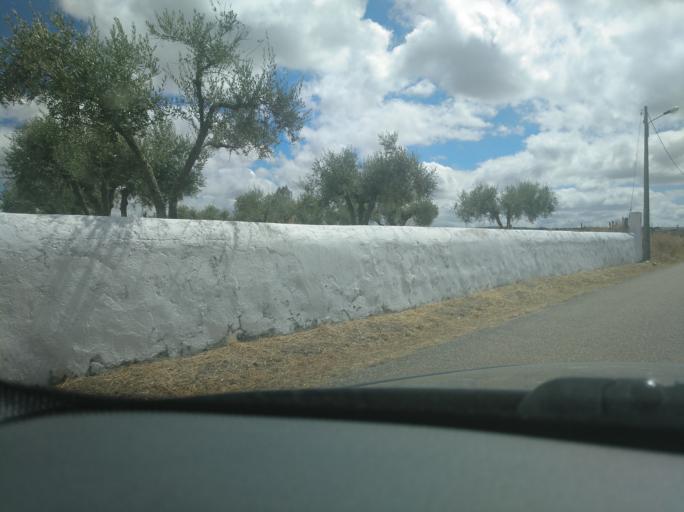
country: PT
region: Portalegre
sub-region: Arronches
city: Arronches
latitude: 39.0133
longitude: -7.2415
